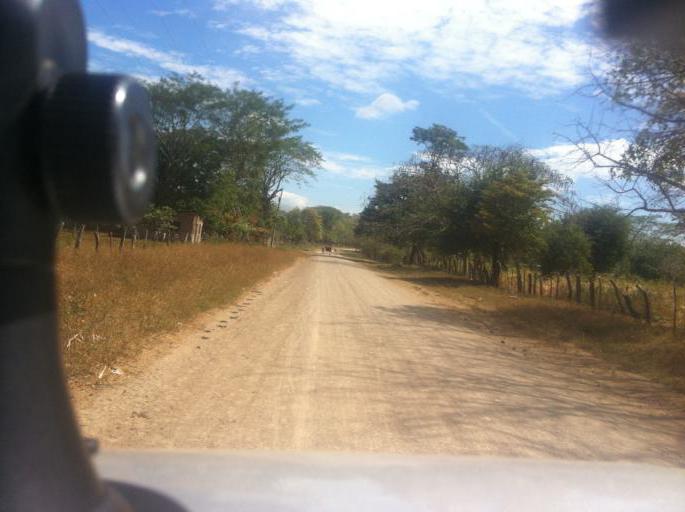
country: NI
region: Granada
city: Nandaime
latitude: 11.6045
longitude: -86.0306
